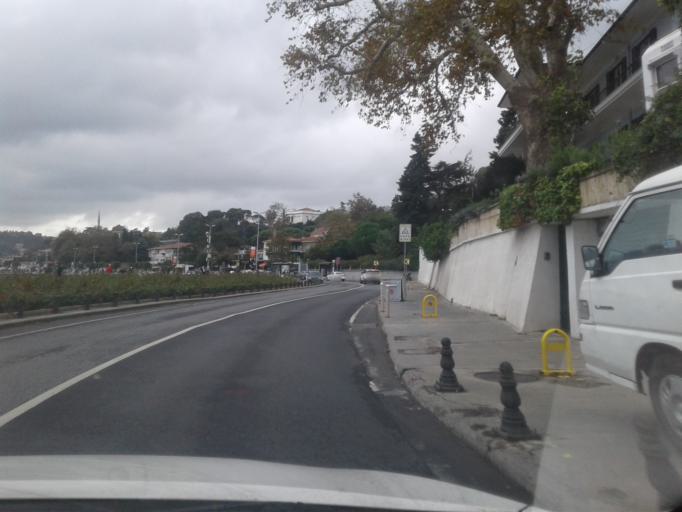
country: TR
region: Istanbul
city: Sisli
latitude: 41.1084
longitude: 29.0589
